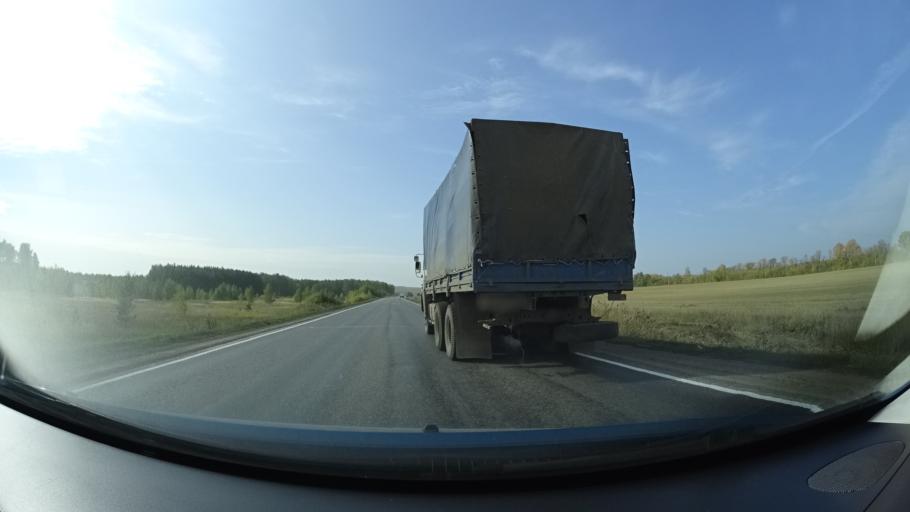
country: RU
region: Bashkortostan
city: Kandry
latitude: 54.6118
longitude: 54.3182
